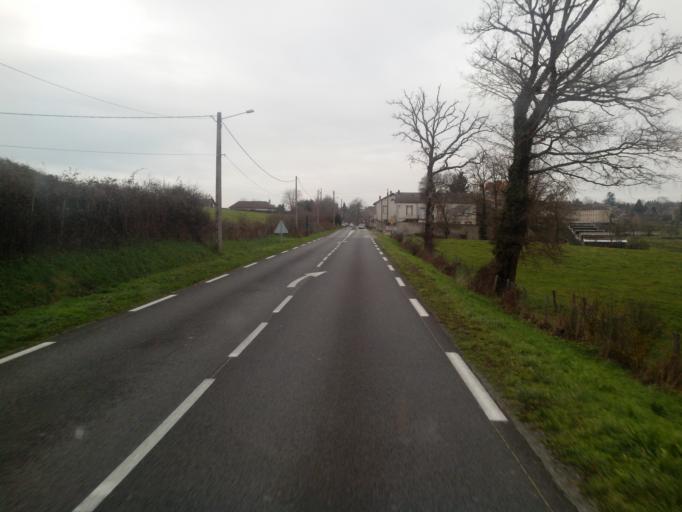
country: FR
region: Limousin
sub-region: Departement de la Haute-Vienne
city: Magnac-Laval
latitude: 46.2115
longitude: 1.1761
